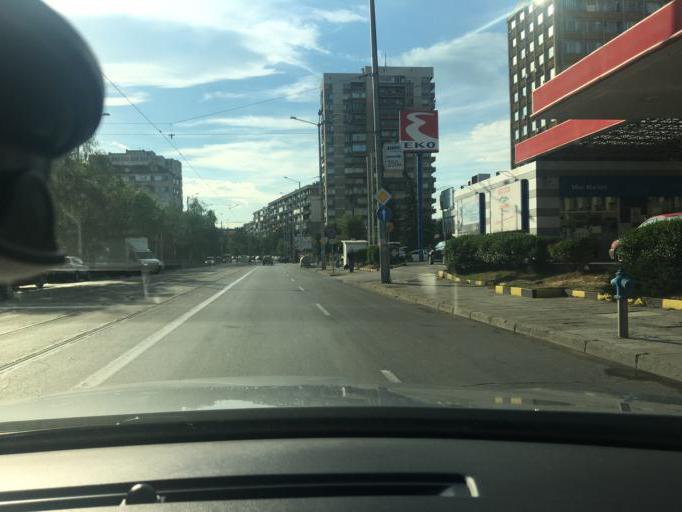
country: BG
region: Sofia-Capital
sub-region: Stolichna Obshtina
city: Sofia
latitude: 42.6779
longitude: 23.3671
